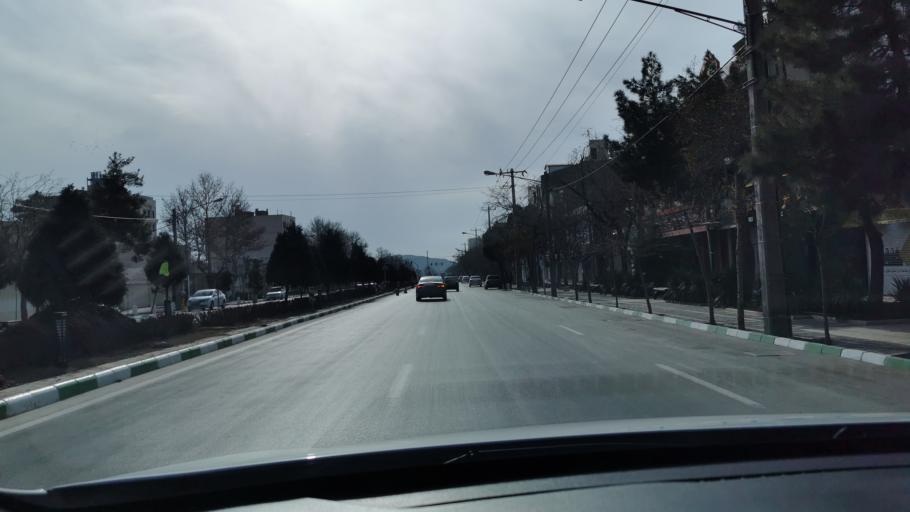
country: IR
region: Razavi Khorasan
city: Mashhad
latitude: 36.2886
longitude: 59.5418
